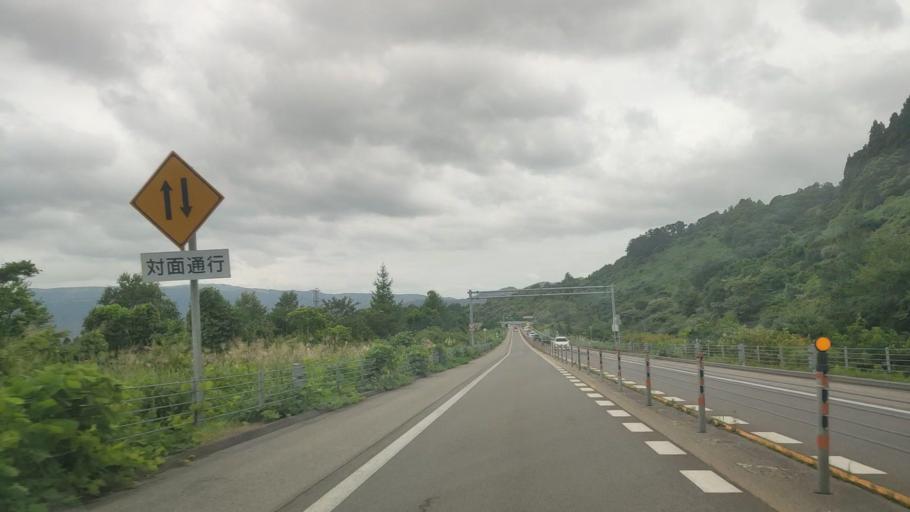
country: JP
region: Hokkaido
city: Nanae
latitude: 41.9104
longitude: 140.6936
